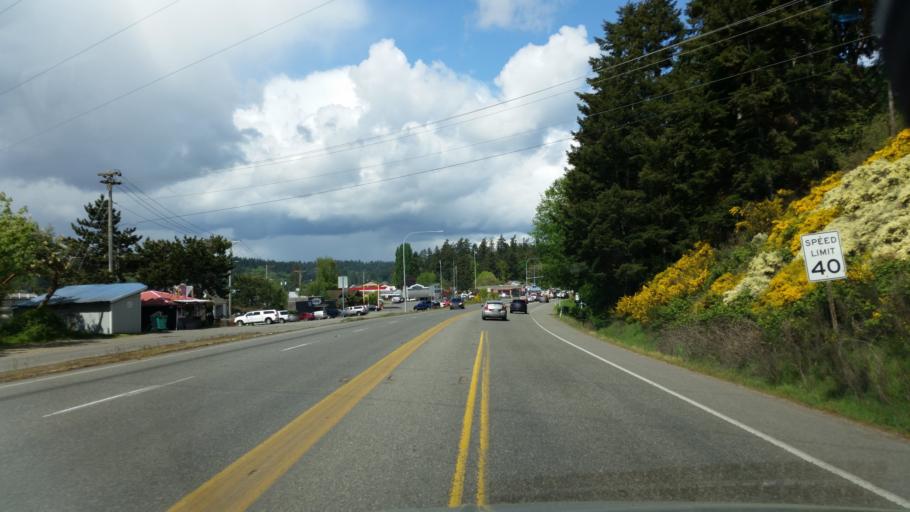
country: US
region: Washington
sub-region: Pierce County
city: Purdy
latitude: 47.3824
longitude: -122.6255
